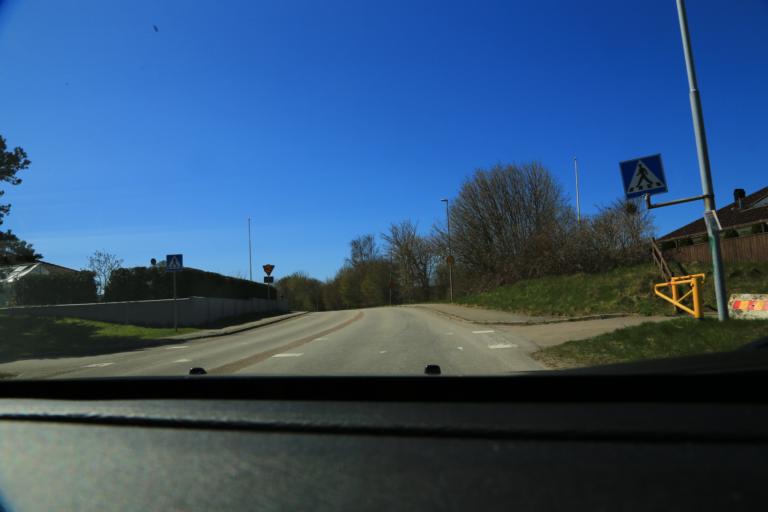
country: SE
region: Halland
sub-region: Varbergs Kommun
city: Traslovslage
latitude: 57.1064
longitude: 12.2937
